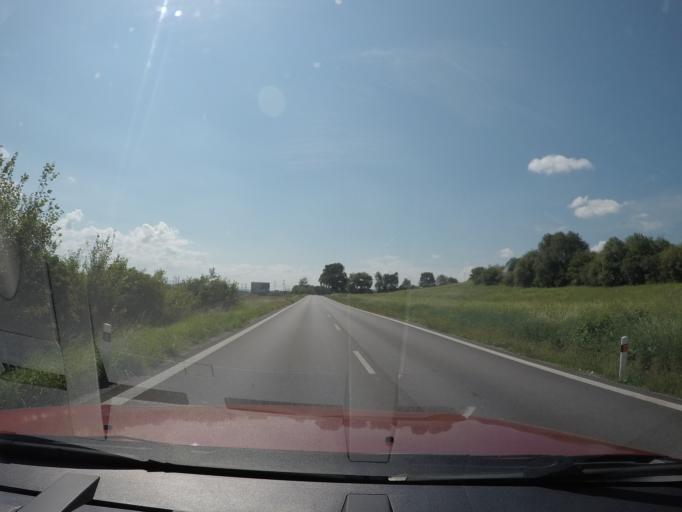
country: SK
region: Presovsky
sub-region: Okres Presov
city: Presov
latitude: 48.8698
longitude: 21.2522
